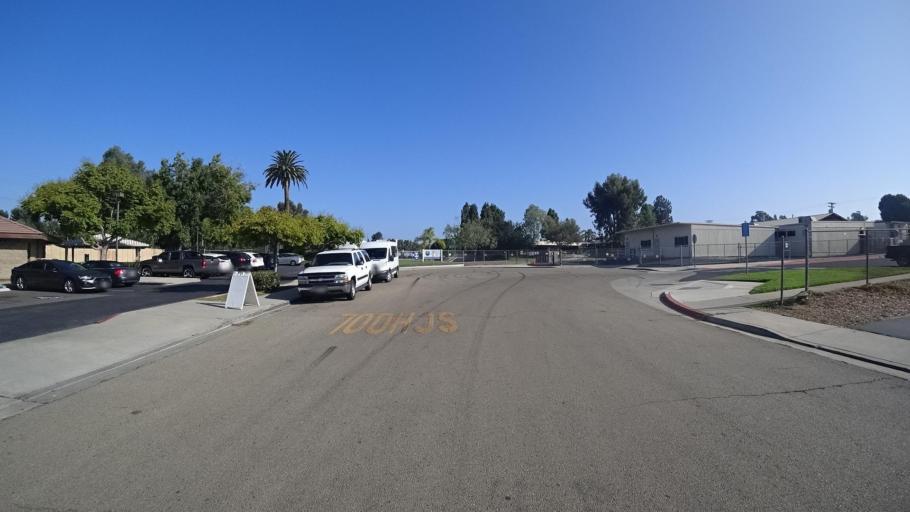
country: US
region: California
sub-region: San Diego County
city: Fallbrook
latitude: 33.3779
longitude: -117.2355
